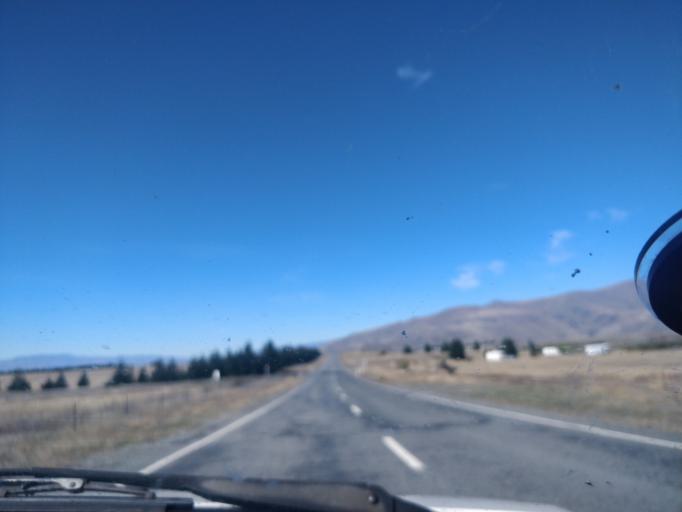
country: NZ
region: Otago
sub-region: Queenstown-Lakes District
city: Wanaka
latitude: -44.2668
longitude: 170.0377
